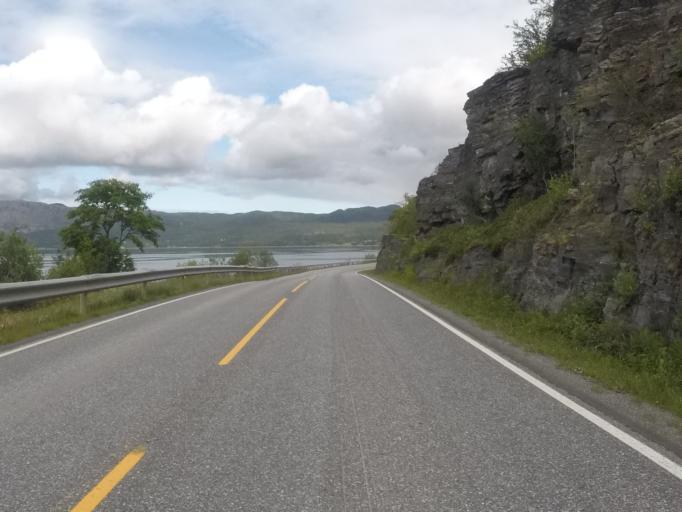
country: NO
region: Finnmark Fylke
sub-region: Alta
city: Alta
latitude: 69.9983
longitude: 23.4787
